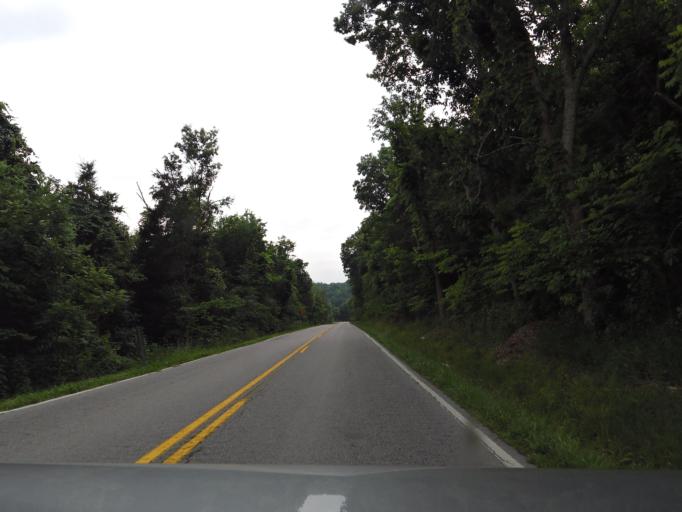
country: US
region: Kentucky
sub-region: Harrison County
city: Cynthiana
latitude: 38.5103
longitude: -84.2061
